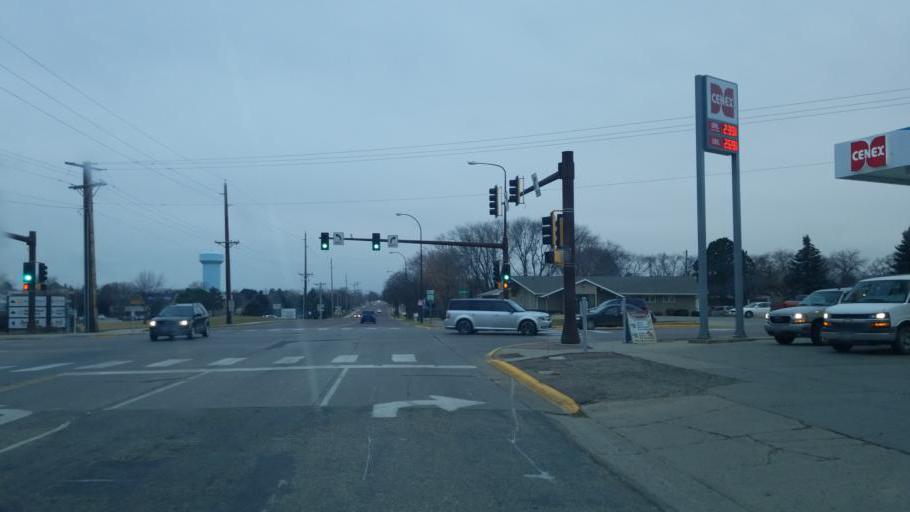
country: US
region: South Dakota
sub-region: Yankton County
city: Yankton
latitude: 42.8763
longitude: -97.4070
